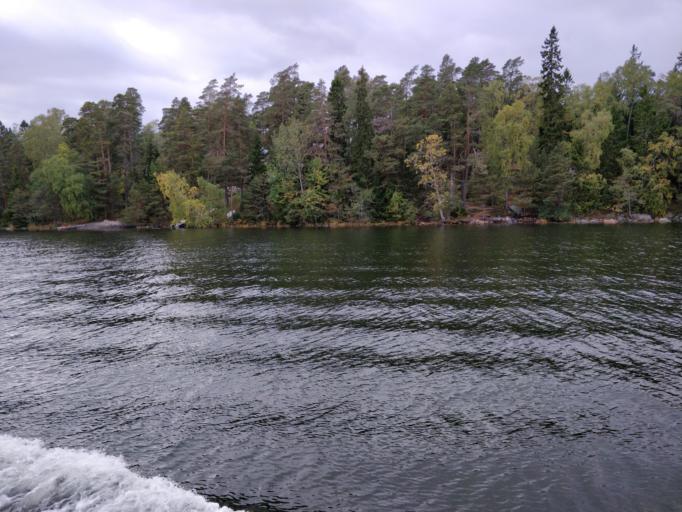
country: FI
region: Uusimaa
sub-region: Helsinki
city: Vantaa
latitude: 60.1640
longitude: 25.0989
